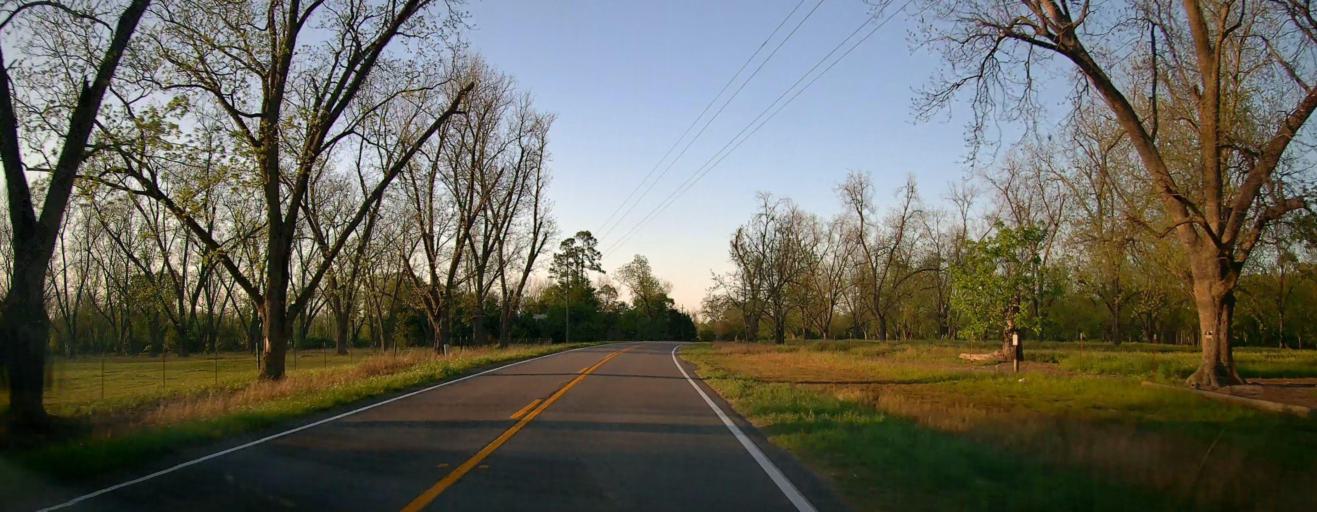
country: US
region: Georgia
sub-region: Irwin County
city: Ocilla
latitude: 31.6363
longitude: -83.2754
